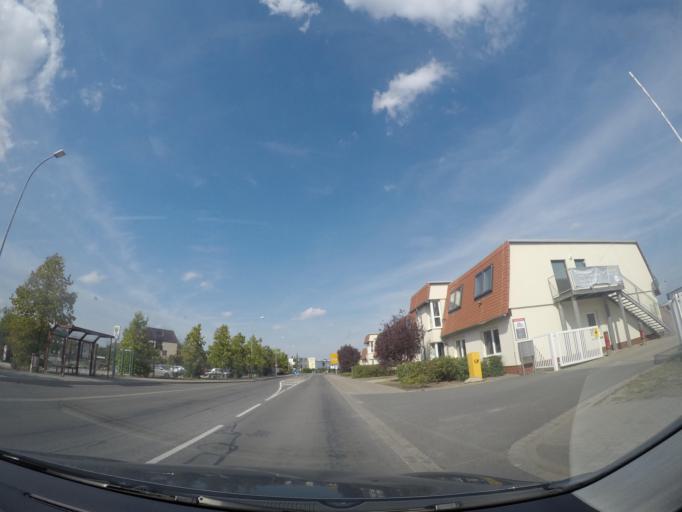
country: DE
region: Saxony-Anhalt
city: Wernigerode
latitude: 51.8455
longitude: 10.7831
